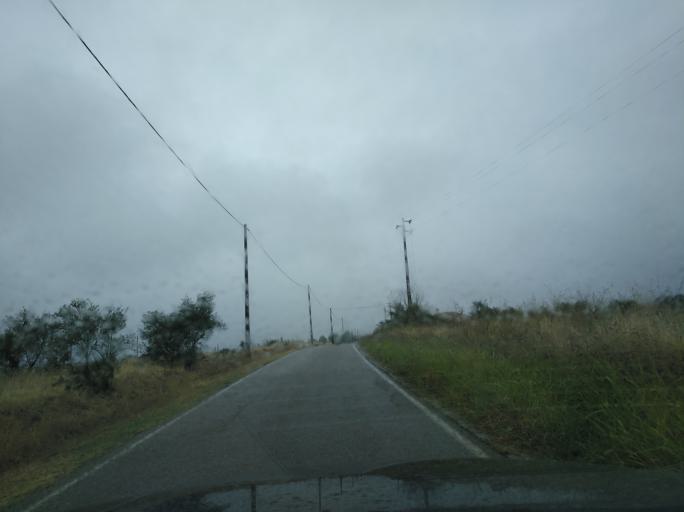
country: PT
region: Portalegre
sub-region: Campo Maior
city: Campo Maior
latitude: 38.9564
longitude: -7.0831
